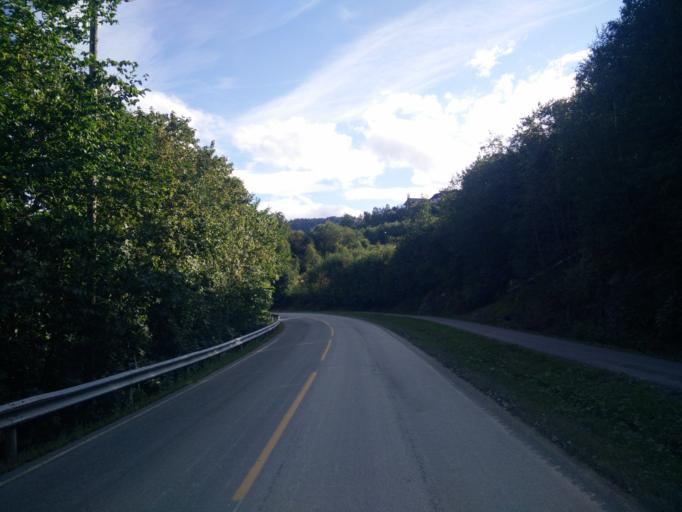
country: NO
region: Sor-Trondelag
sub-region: Skaun
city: Borsa
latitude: 63.3128
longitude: 10.1588
